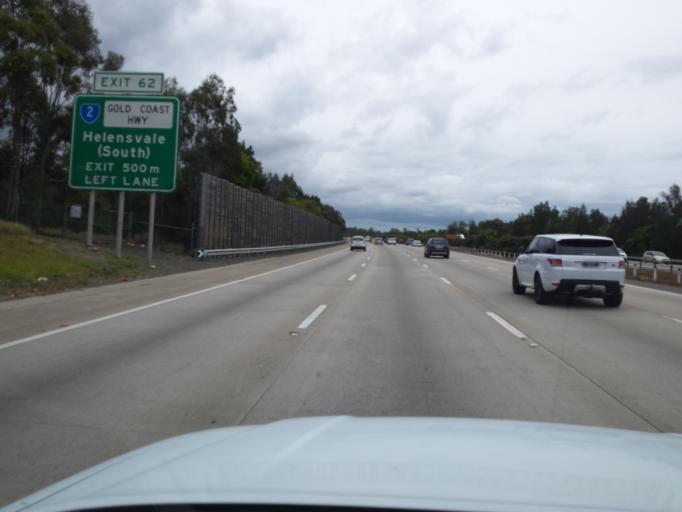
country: AU
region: Queensland
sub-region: Gold Coast
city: Upper Coomera
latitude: -27.9356
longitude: 153.3354
